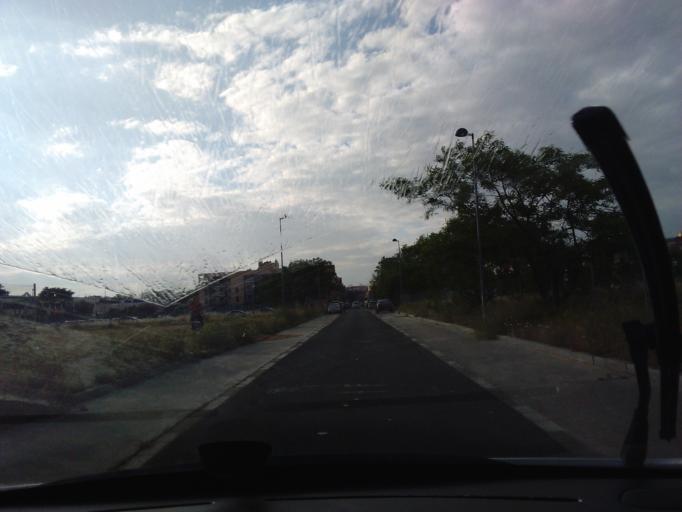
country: ES
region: Andalusia
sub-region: Provincia de Sevilla
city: Sevilla
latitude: 37.3938
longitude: -5.9226
